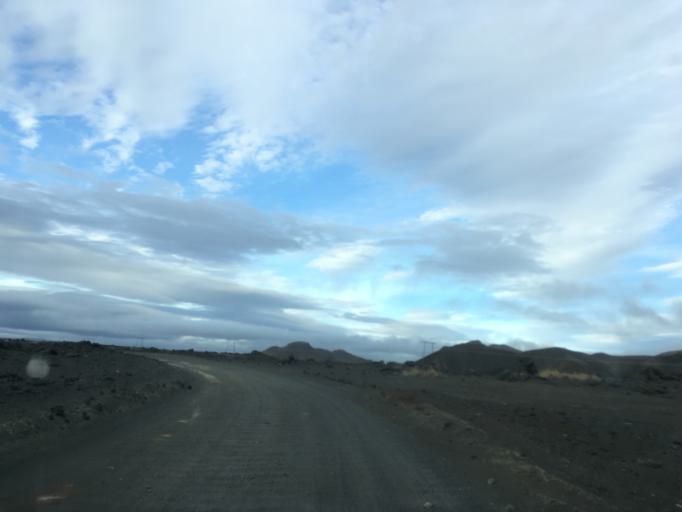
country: IS
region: South
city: Vestmannaeyjar
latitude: 64.0986
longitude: -19.1079
